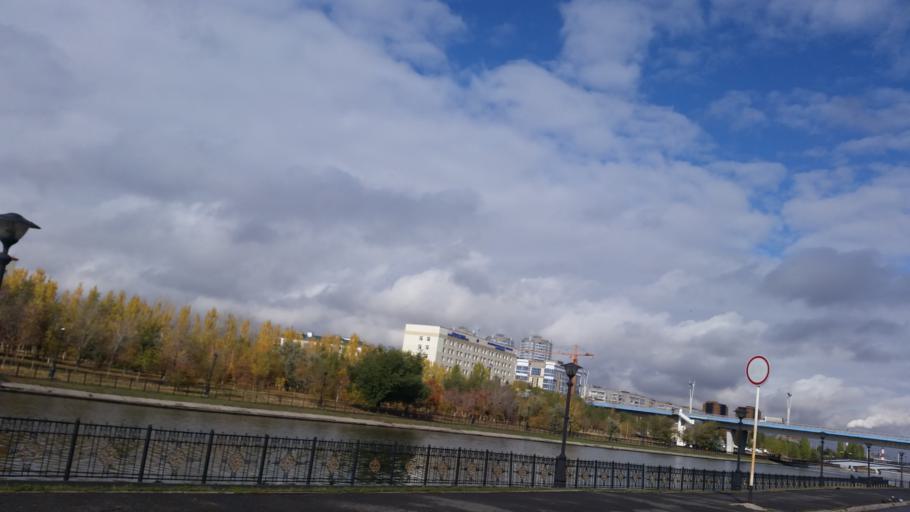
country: KZ
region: Astana Qalasy
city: Astana
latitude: 51.1569
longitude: 71.4635
